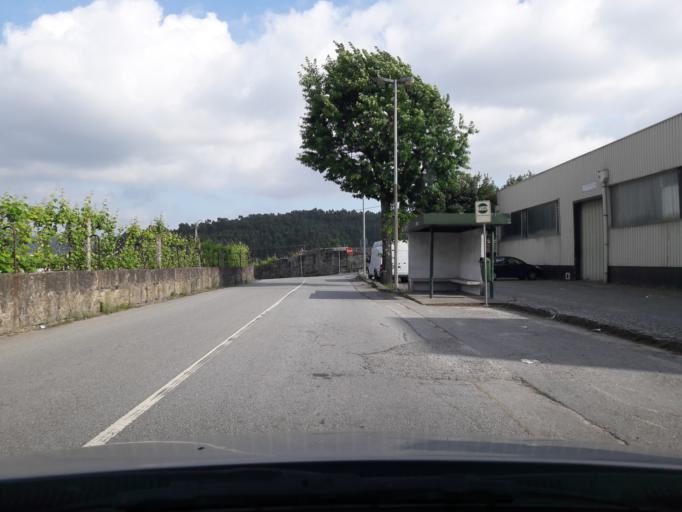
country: PT
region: Braga
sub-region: Guimaraes
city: Selho
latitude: 41.4239
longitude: -8.3342
